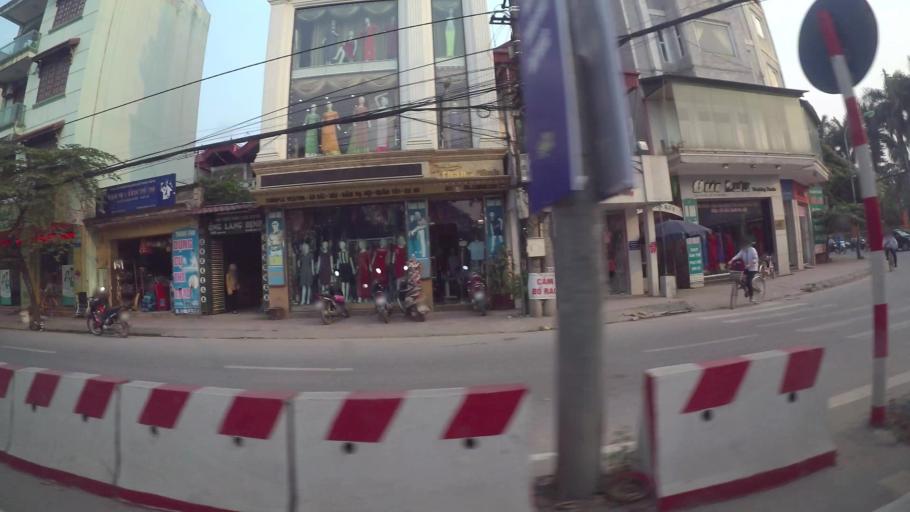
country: VN
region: Ha Noi
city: Thuong Tin
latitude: 20.8684
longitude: 105.8627
